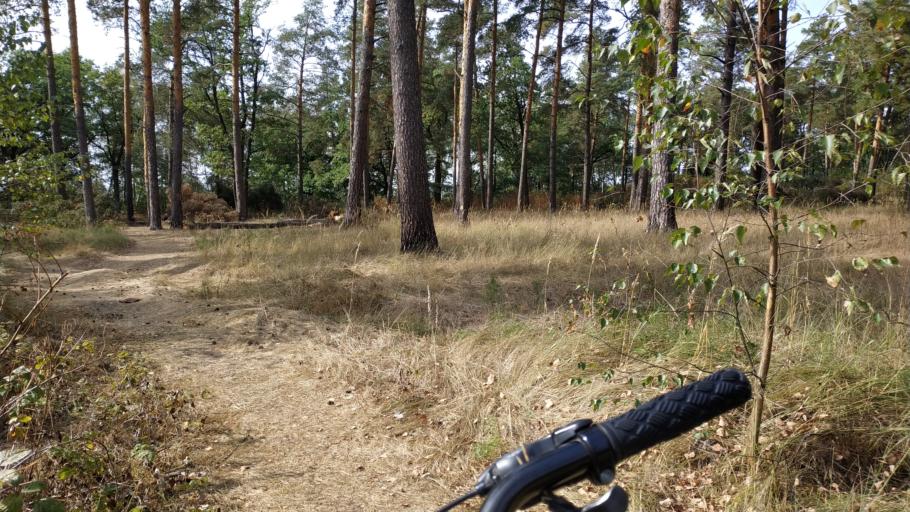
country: RU
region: Moskovskaya
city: Ramenskoye
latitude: 55.5349
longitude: 38.2905
